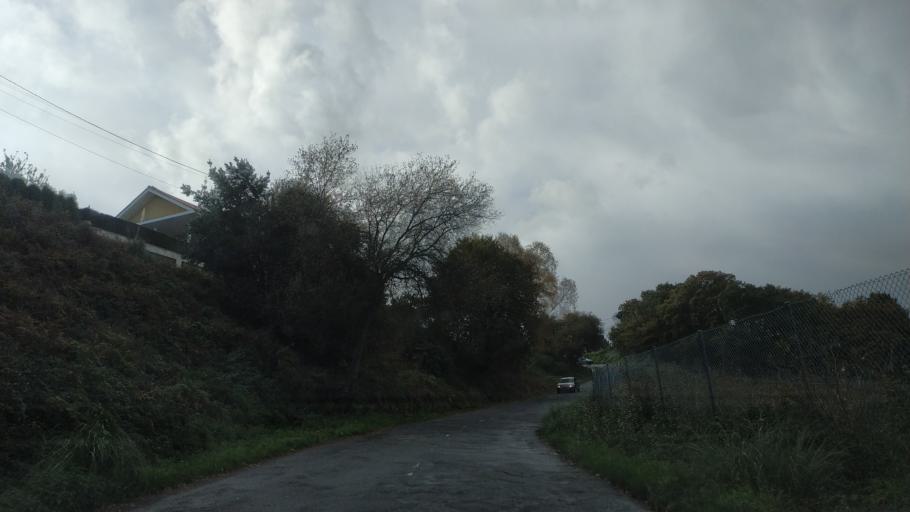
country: ES
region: Galicia
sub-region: Provincia da Coruna
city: Culleredo
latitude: 43.3278
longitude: -8.3974
